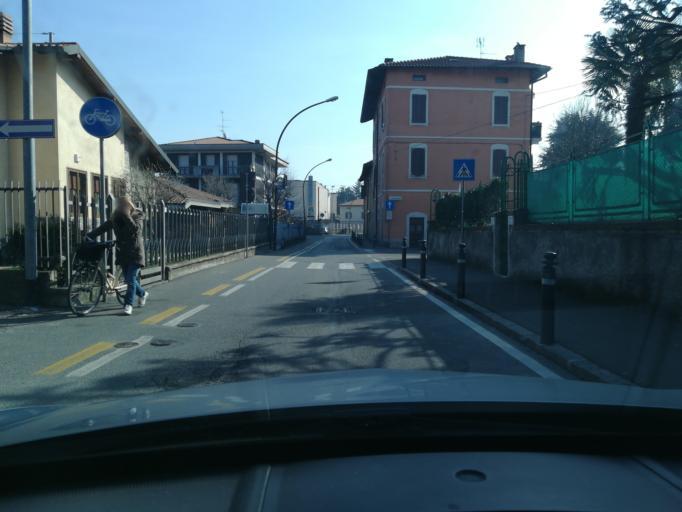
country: IT
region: Lombardy
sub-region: Provincia di Bergamo
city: Stezzano
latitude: 45.6534
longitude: 9.6519
